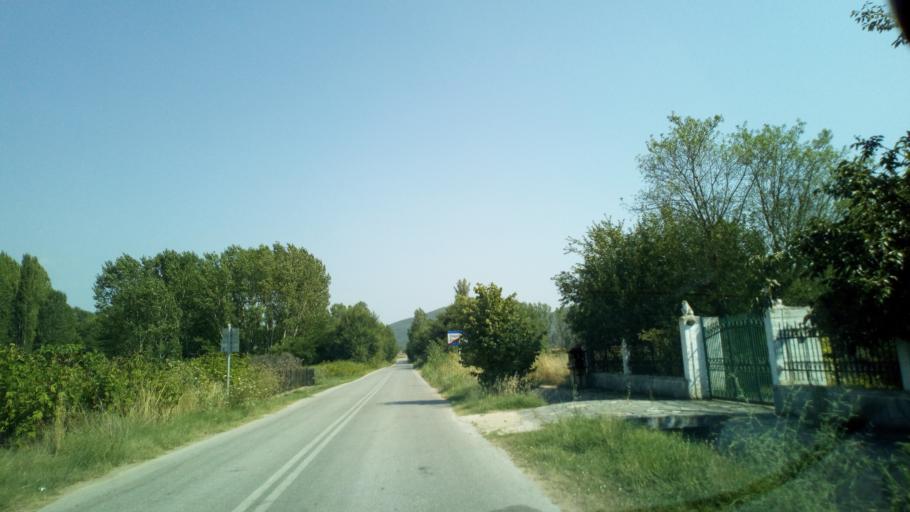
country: GR
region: Central Macedonia
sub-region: Nomos Thessalonikis
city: Gerakarou
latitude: 40.5668
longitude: 23.2890
